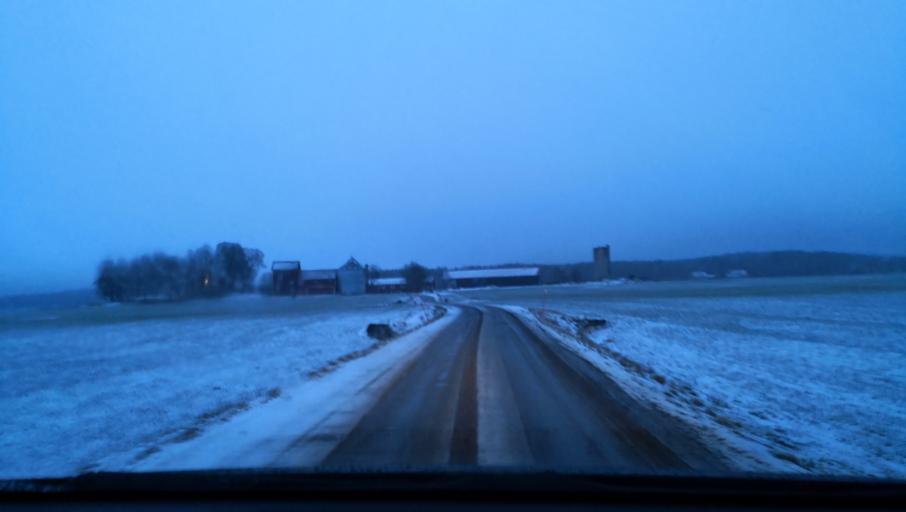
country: SE
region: Soedermanland
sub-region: Eskilstuna Kommun
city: Kvicksund
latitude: 59.3724
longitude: 16.2947
